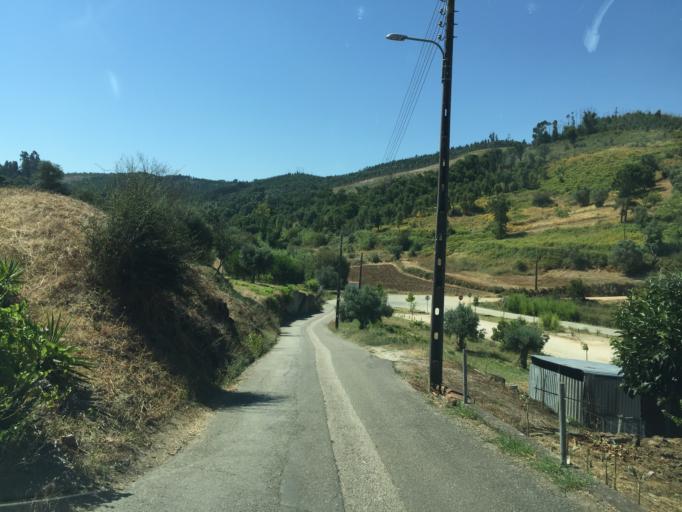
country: PT
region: Santarem
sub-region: Constancia
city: Constancia
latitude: 39.5441
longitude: -8.2749
